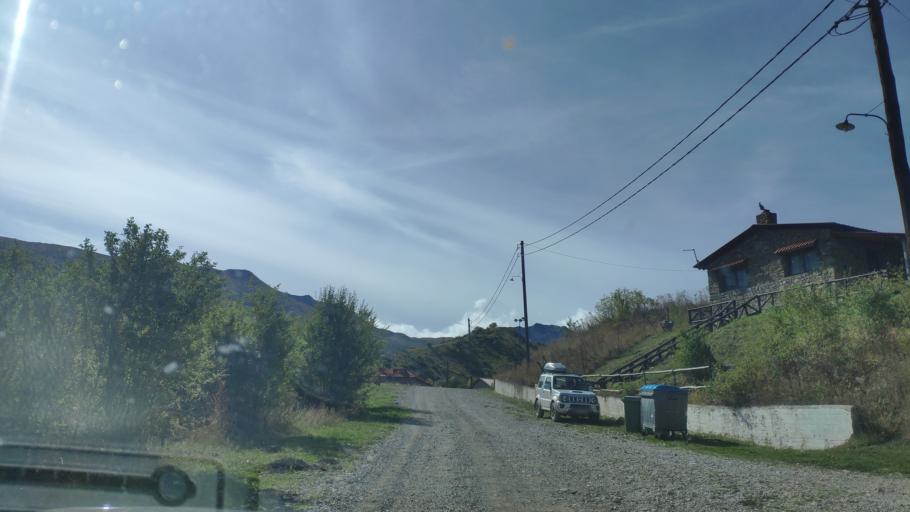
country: AL
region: Korce
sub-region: Rrethi i Devollit
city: Miras
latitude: 40.3926
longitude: 20.8360
